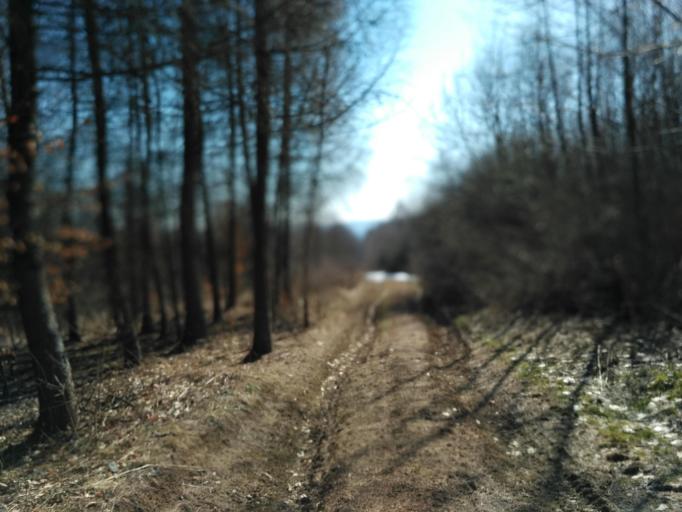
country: PL
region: Subcarpathian Voivodeship
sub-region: Powiat brzozowski
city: Domaradz
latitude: 49.8023
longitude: 21.9612
